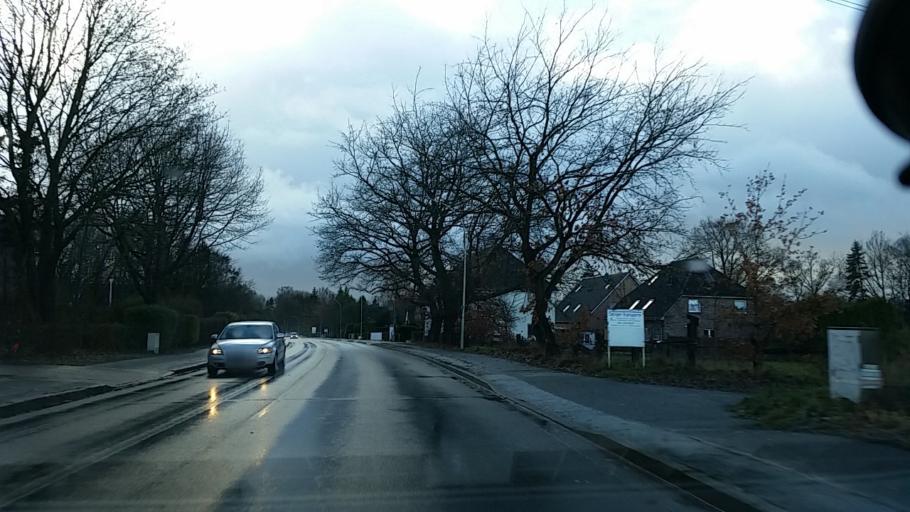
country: DE
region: Schleswig-Holstein
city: Halstenbek
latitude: 53.5876
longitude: 9.8233
